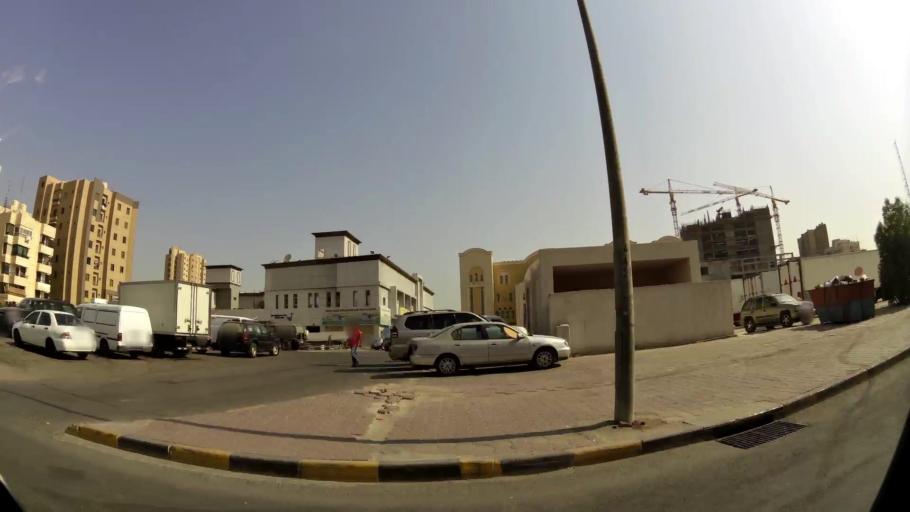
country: KW
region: Muhafazat Hawalli
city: Hawalli
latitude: 29.3379
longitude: 48.0160
